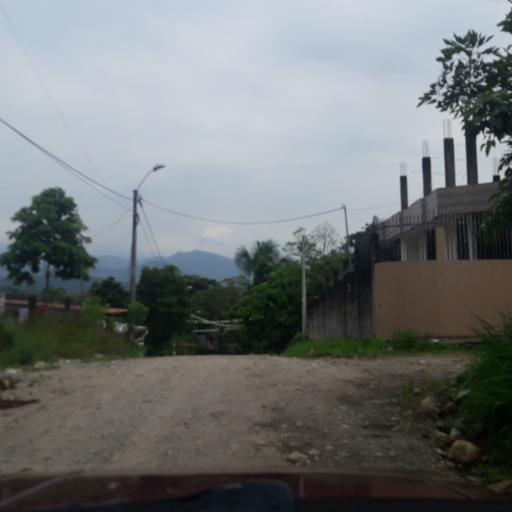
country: EC
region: Napo
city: Tena
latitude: -0.9798
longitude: -77.8161
